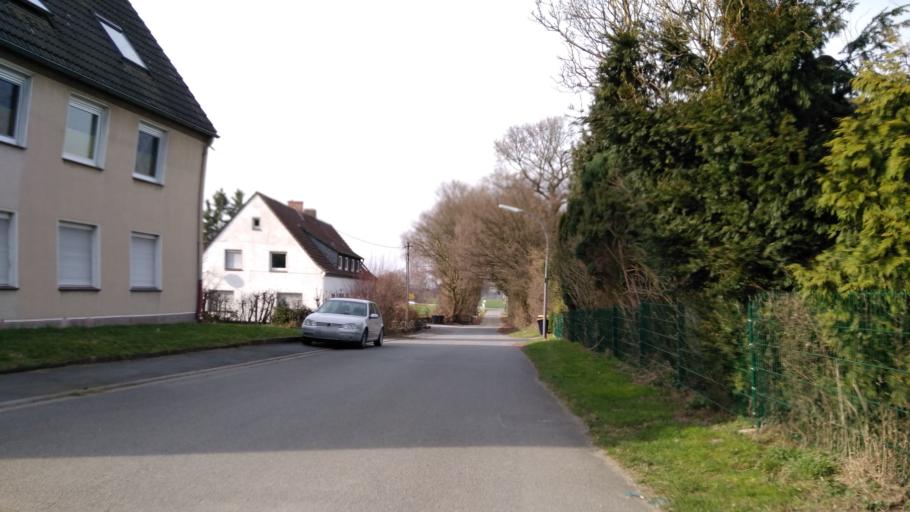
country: DE
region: North Rhine-Westphalia
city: Herten
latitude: 51.6239
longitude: 7.1637
